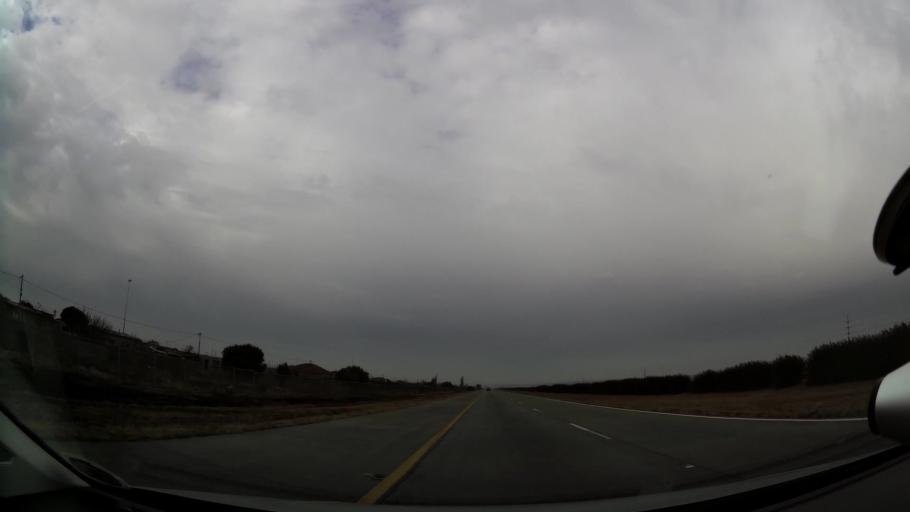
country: ZA
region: Gauteng
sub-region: City of Johannesburg Metropolitan Municipality
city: Orange Farm
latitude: -26.5150
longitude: 27.8114
